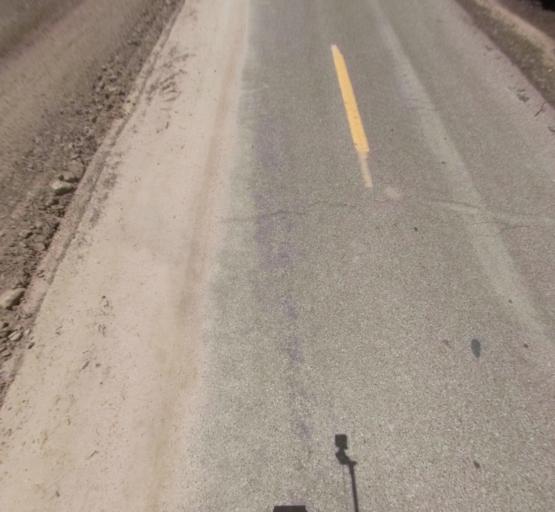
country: US
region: California
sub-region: Madera County
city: Parkwood
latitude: 36.9165
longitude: -120.1003
